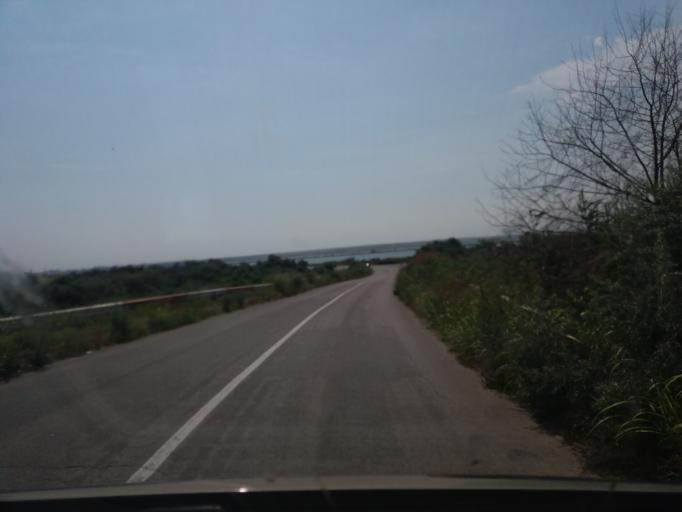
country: RO
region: Constanta
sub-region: Comuna Corbu
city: Corbu
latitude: 44.3520
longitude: 28.6520
